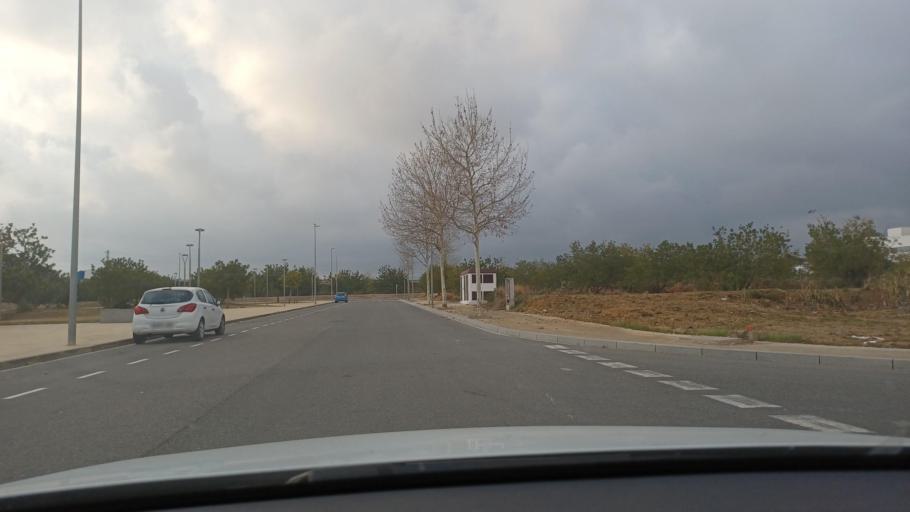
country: ES
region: Catalonia
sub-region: Provincia de Tarragona
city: Vila-seca
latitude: 41.1202
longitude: 1.1493
